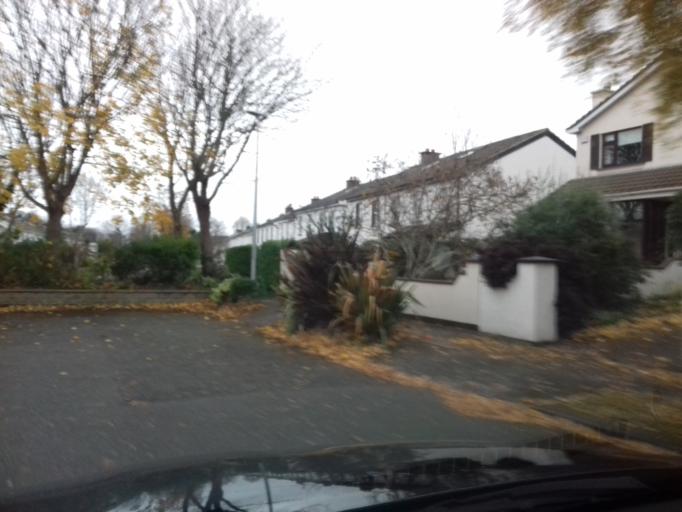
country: IE
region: Leinster
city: Malahide
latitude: 53.4488
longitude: -6.1429
